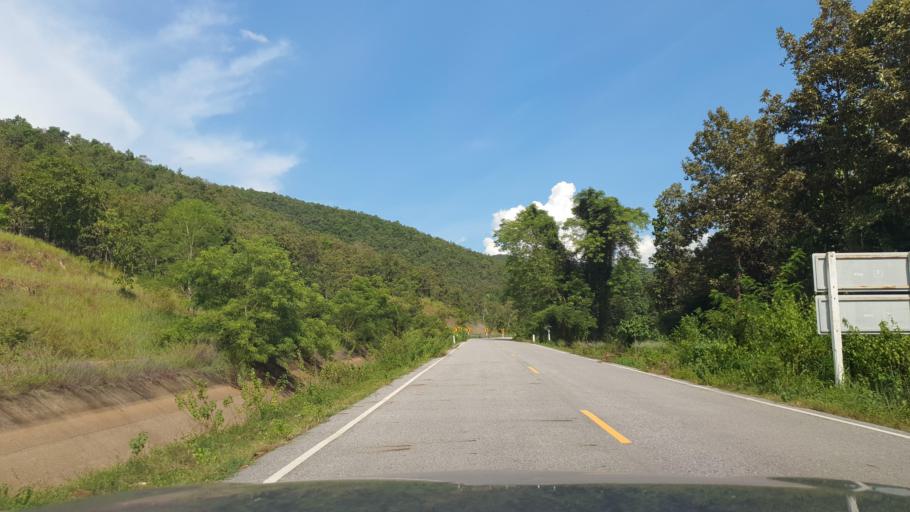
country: TH
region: Chiang Mai
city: San Kamphaeng
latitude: 18.7700
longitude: 99.1757
